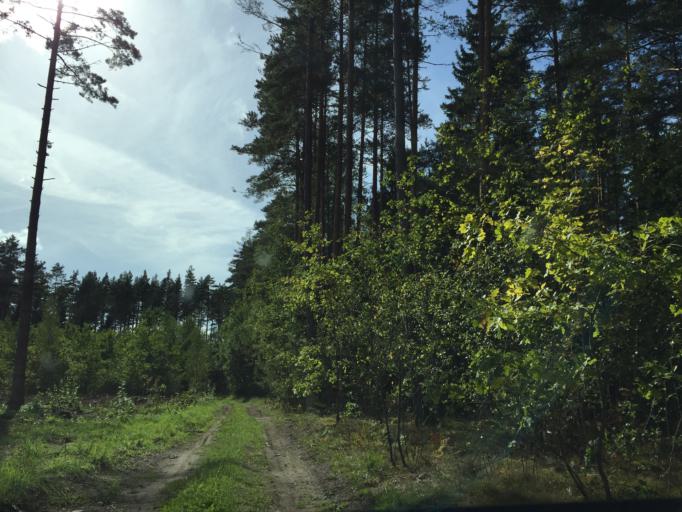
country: LV
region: Kuldigas Rajons
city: Kuldiga
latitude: 56.9935
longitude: 21.8141
